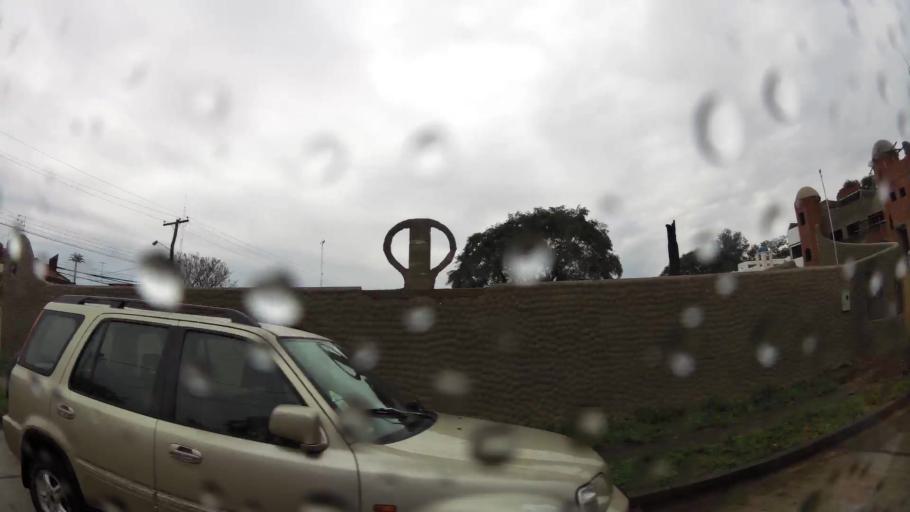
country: BO
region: Santa Cruz
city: Santa Cruz de la Sierra
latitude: -17.8076
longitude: -63.2005
